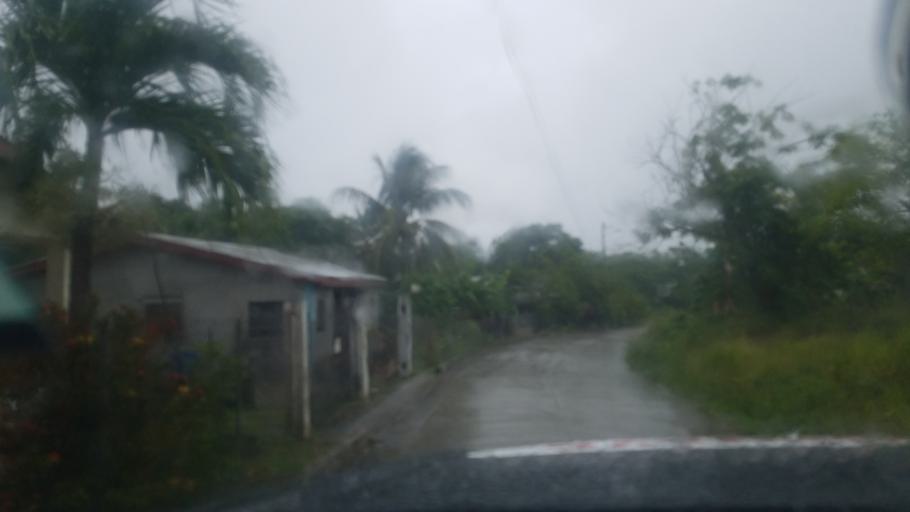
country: LC
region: Laborie Quarter
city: Laborie
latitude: 13.7588
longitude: -60.9775
